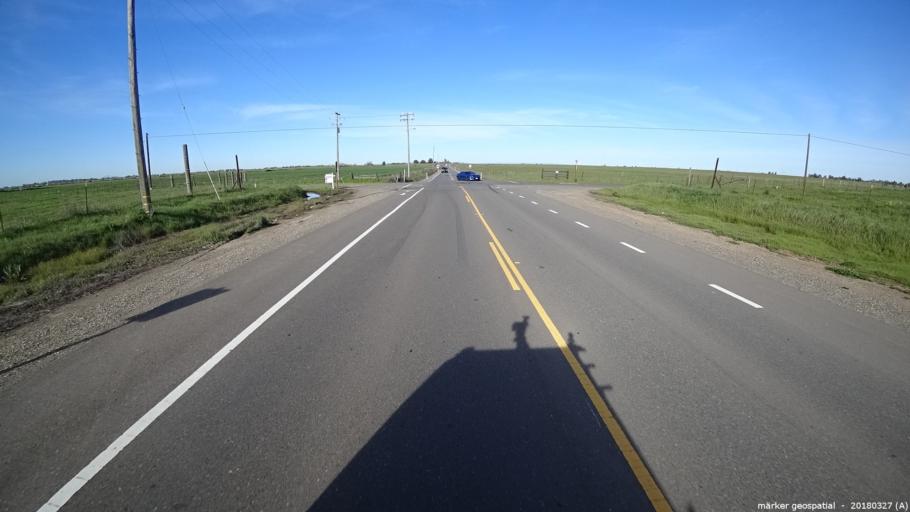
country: US
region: California
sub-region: Sacramento County
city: Wilton
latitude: 38.4966
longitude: -121.2606
